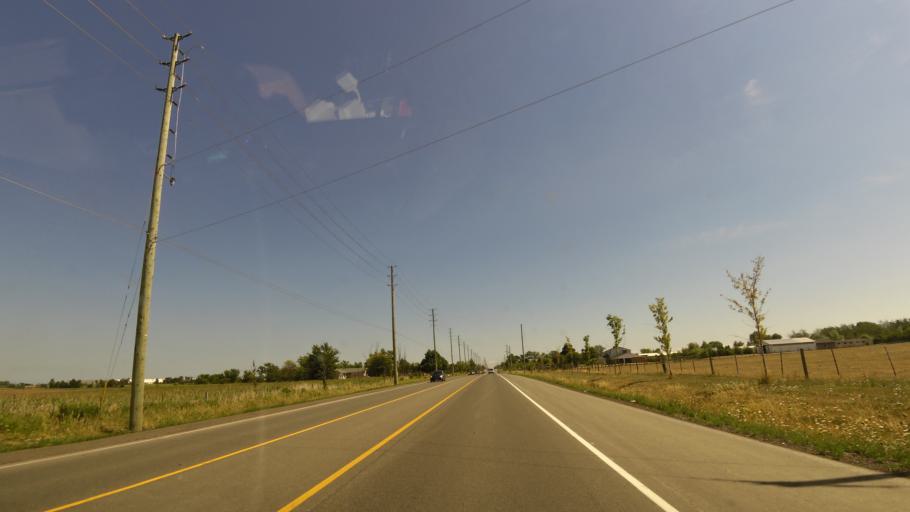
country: CA
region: Ontario
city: Brampton
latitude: 43.6204
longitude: -79.8153
